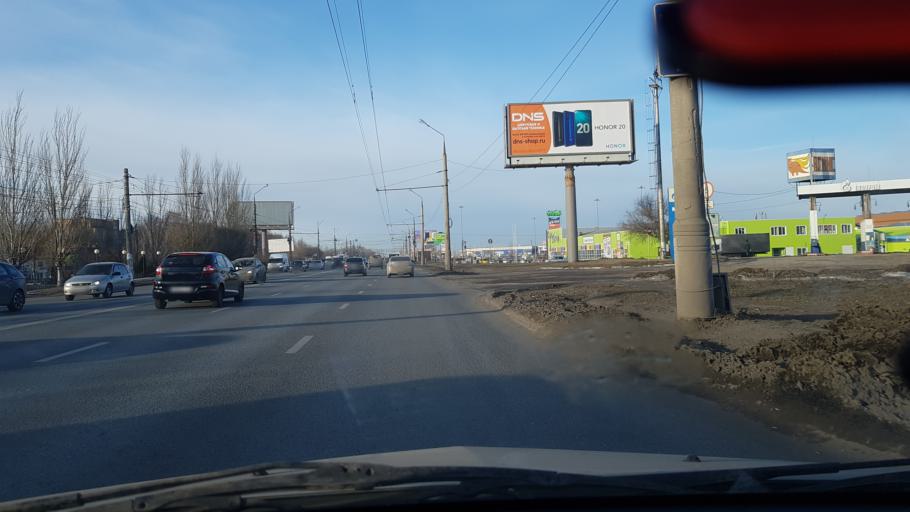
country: RU
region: Samara
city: Tol'yatti
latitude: 53.5378
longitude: 49.3914
